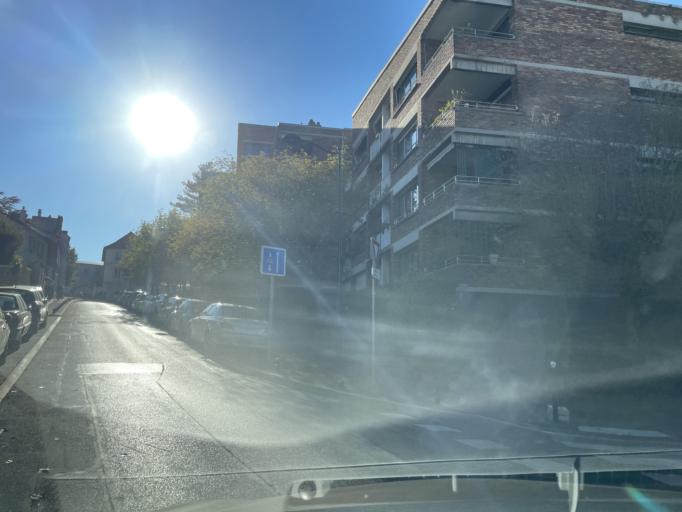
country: FR
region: Ile-de-France
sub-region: Departement du Val-de-Marne
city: Joinville-le-Pont
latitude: 48.8143
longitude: 2.4725
